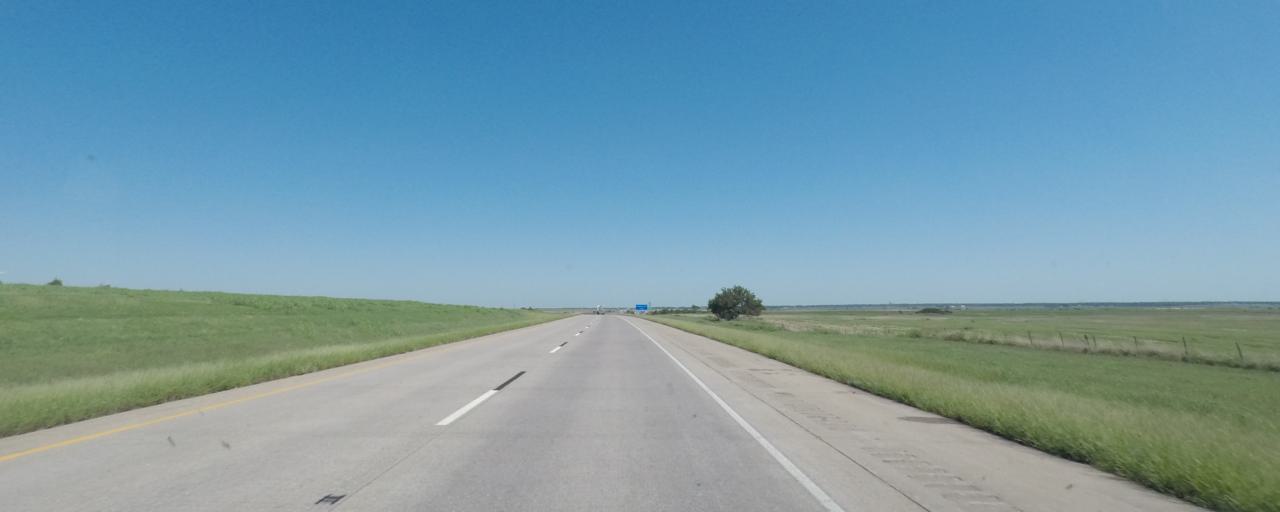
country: US
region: Oklahoma
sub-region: Kay County
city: Tonkawa
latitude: 36.5944
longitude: -97.3453
